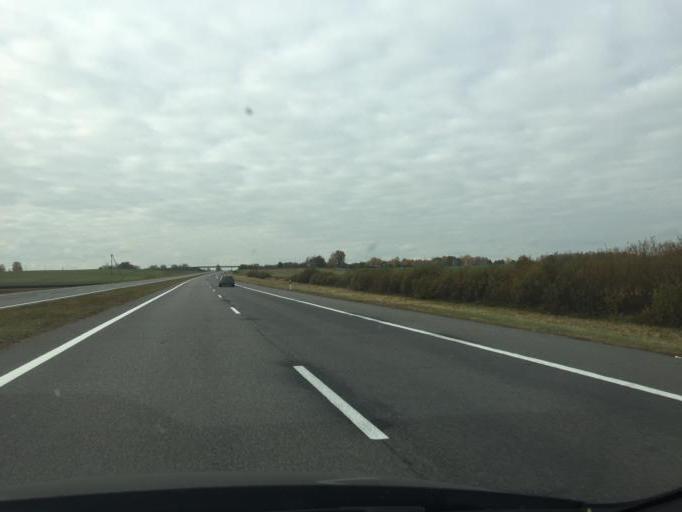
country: BY
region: Minsk
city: Stan'kava
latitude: 53.6758
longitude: 27.2237
